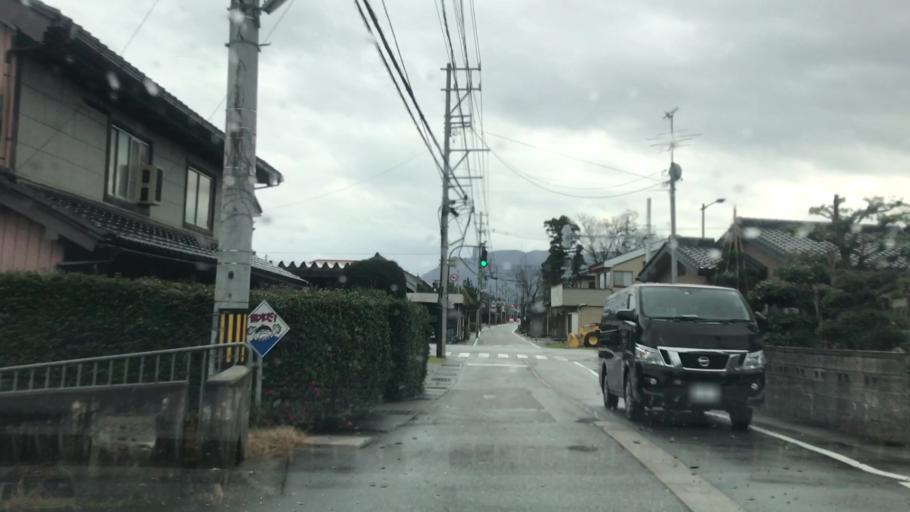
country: JP
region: Toyama
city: Yatsuomachi-higashikumisaka
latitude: 36.5927
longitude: 137.2068
